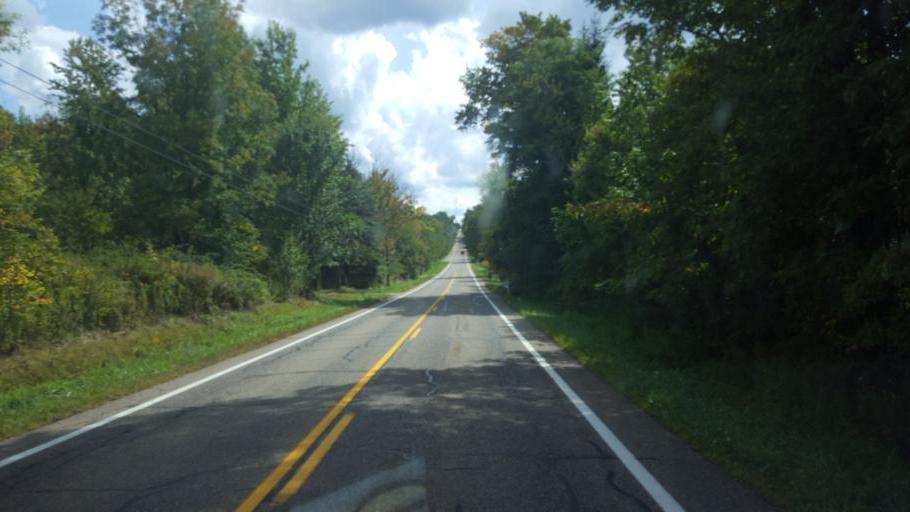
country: US
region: Ohio
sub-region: Portage County
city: Hiram
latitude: 41.3198
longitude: -81.1434
